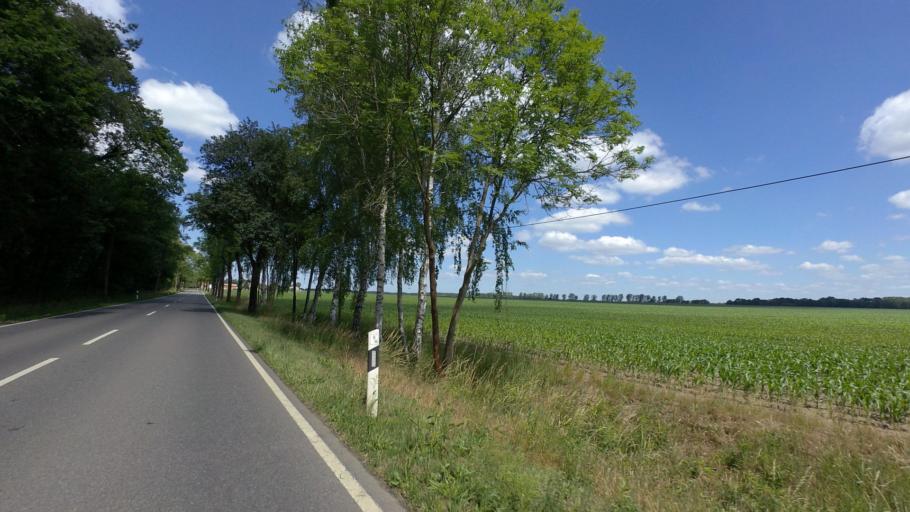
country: DE
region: Brandenburg
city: Luckau
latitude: 51.7970
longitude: 13.6862
